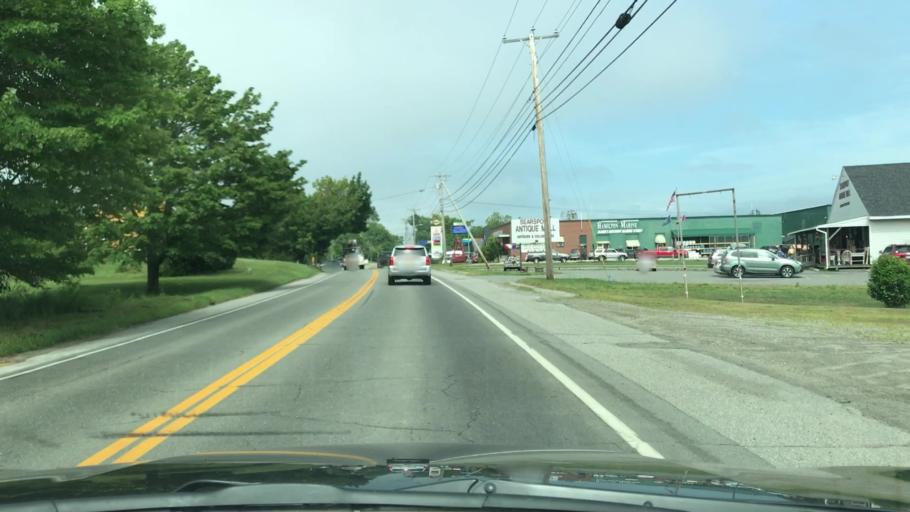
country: US
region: Maine
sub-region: Waldo County
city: Stockton Springs
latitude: 44.4597
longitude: -68.9121
